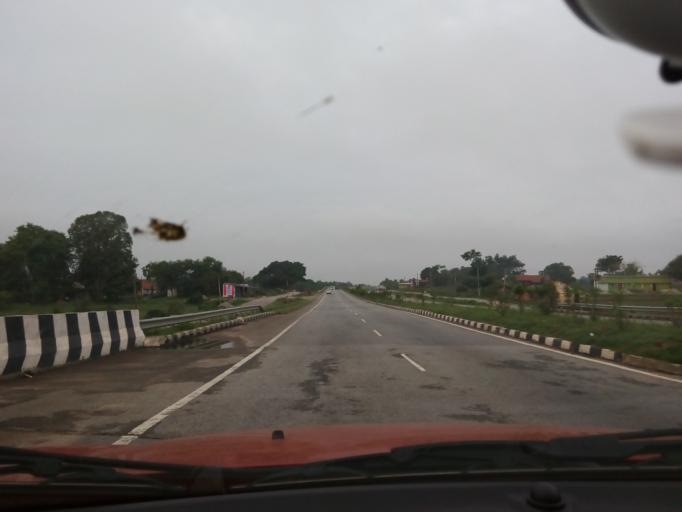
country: IN
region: Karnataka
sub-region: Tumkur
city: Kunigal
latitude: 13.0021
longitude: 76.9675
